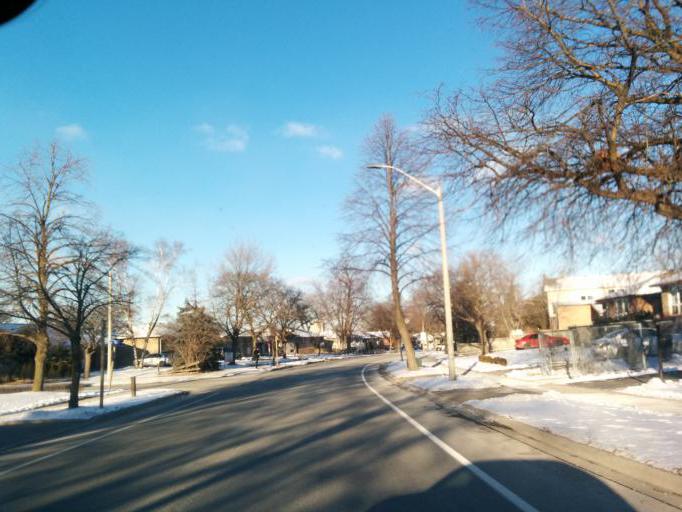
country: CA
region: Ontario
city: Oakville
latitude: 43.5070
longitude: -79.6561
